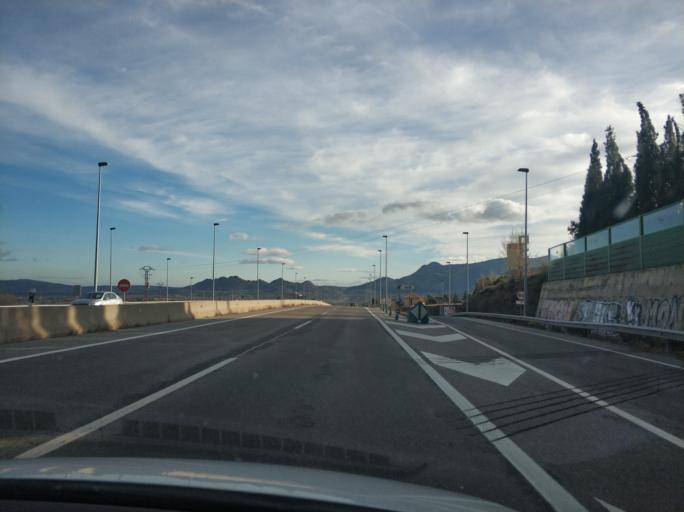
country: ES
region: Madrid
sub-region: Provincia de Madrid
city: Buitrago del Lozoya
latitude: 40.9356
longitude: -3.6271
